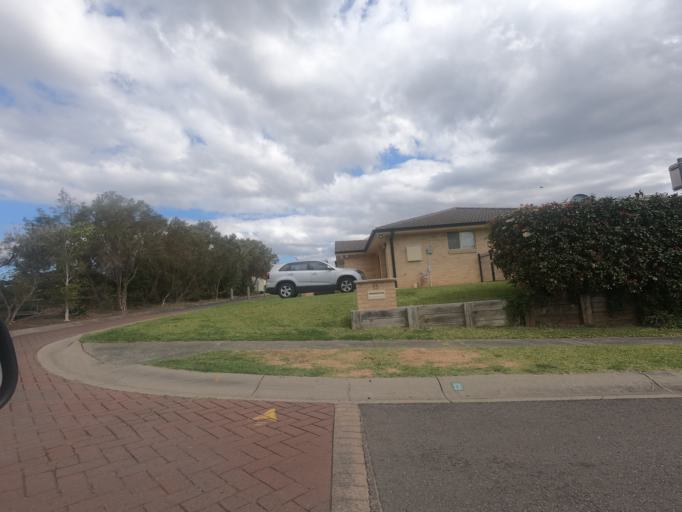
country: AU
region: New South Wales
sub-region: Wollongong
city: Dapto
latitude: -34.4857
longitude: 150.7781
